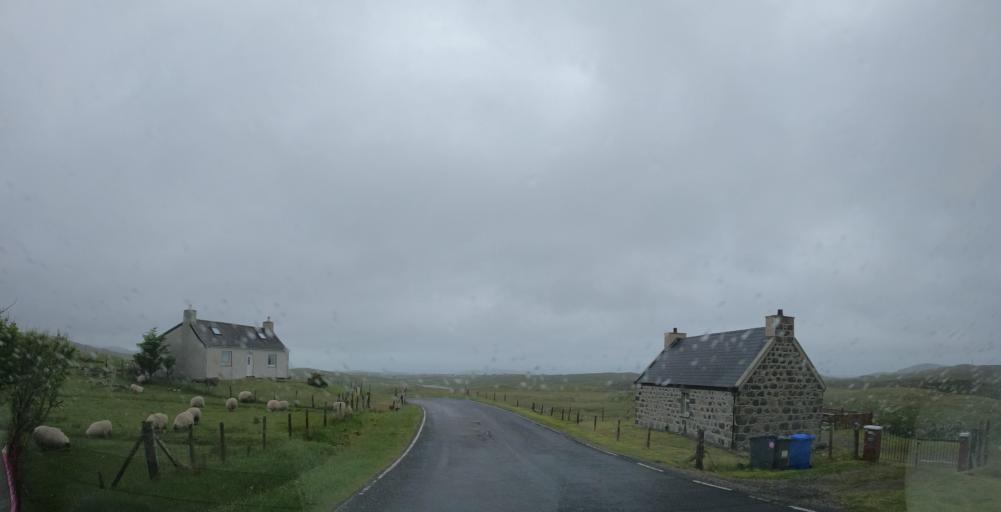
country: GB
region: Scotland
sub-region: Eilean Siar
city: Barra
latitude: 56.9854
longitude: -7.4102
